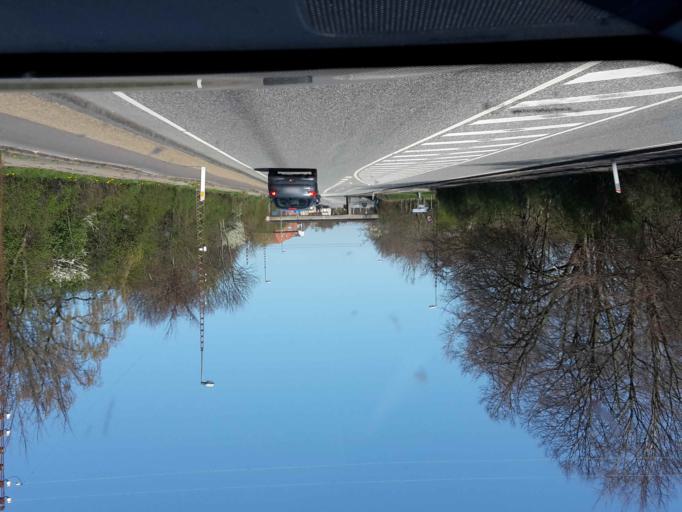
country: DK
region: South Denmark
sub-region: Odense Kommune
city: Odense
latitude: 55.3875
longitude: 10.3528
